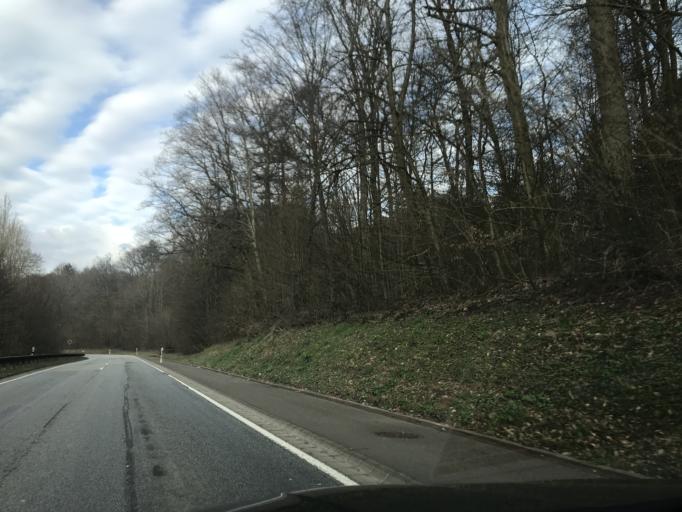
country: DE
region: Saarland
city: Blieskastel
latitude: 49.2131
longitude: 7.2628
